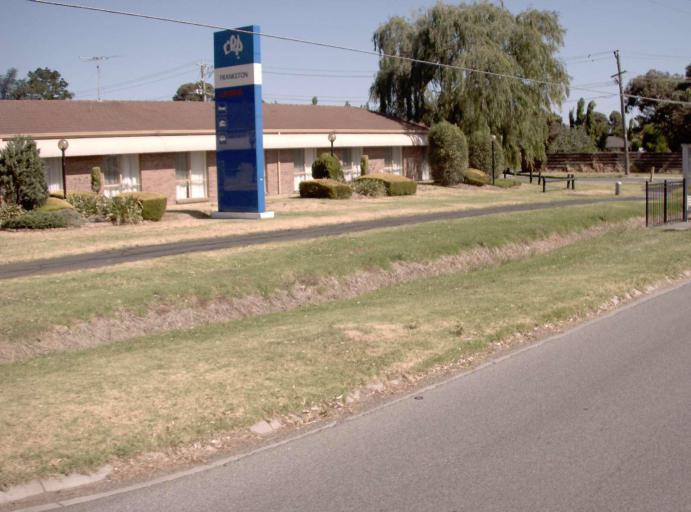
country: AU
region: Victoria
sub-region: Frankston
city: Carrum Downs
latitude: -38.1050
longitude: 145.1683
